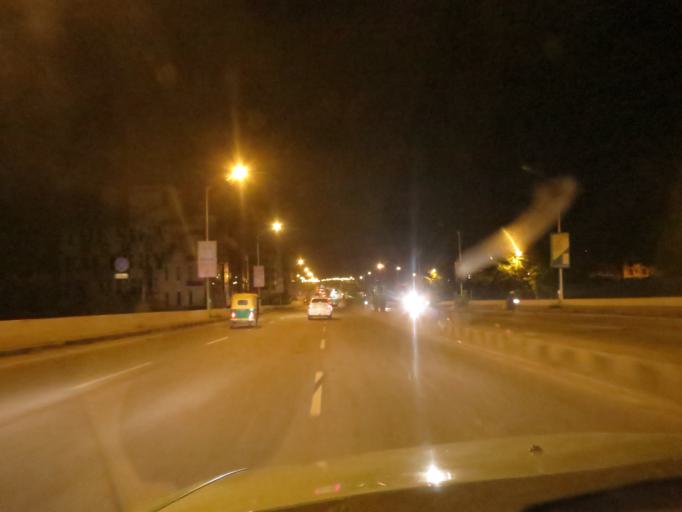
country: IN
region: Karnataka
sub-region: Bangalore Urban
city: Bangalore
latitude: 12.9998
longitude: 77.6634
